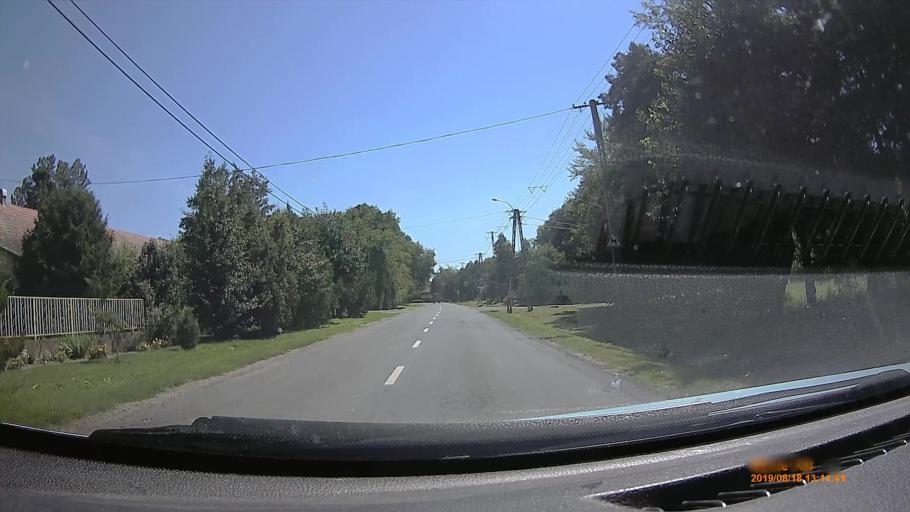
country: HU
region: Fejer
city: Sarbogard
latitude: 46.8736
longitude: 18.5408
